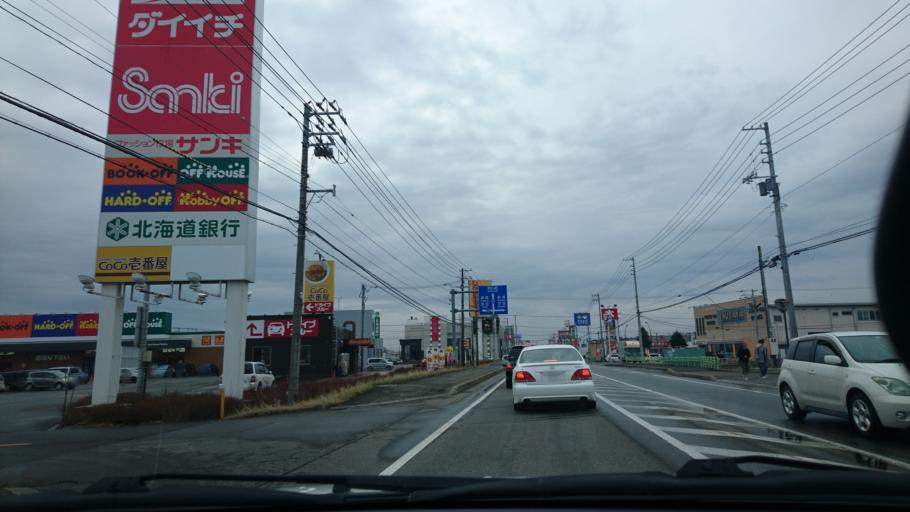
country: JP
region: Hokkaido
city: Otofuke
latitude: 42.9587
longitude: 143.2062
